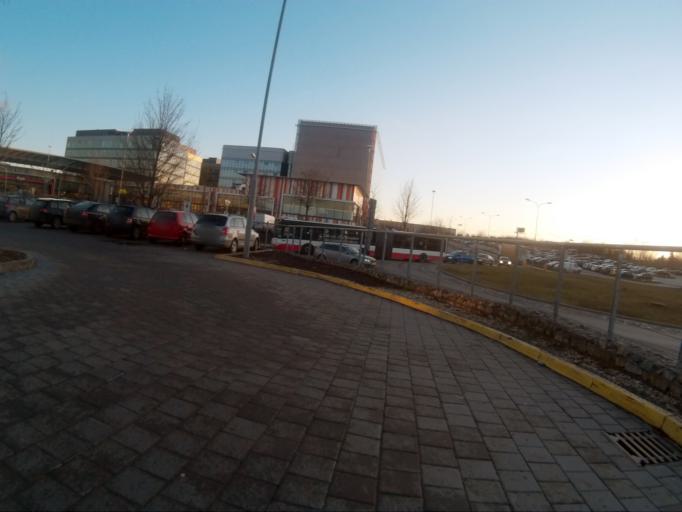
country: CZ
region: South Moravian
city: Ostopovice
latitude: 49.1770
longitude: 16.5650
